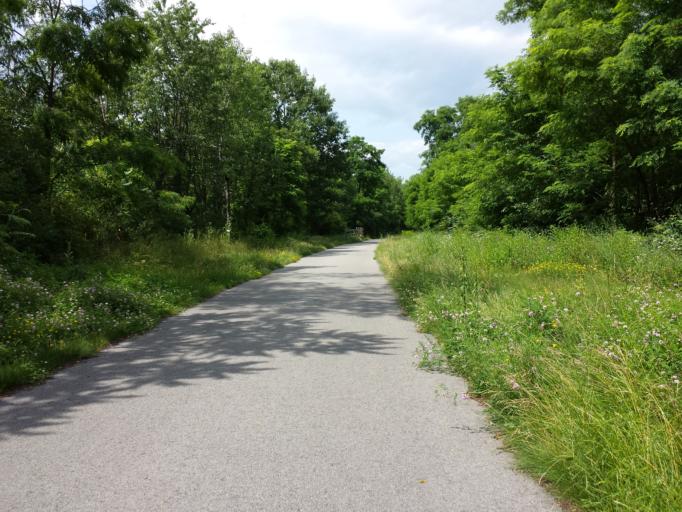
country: US
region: New York
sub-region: Saratoga County
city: Ballston Spa
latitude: 42.9765
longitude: -73.8426
